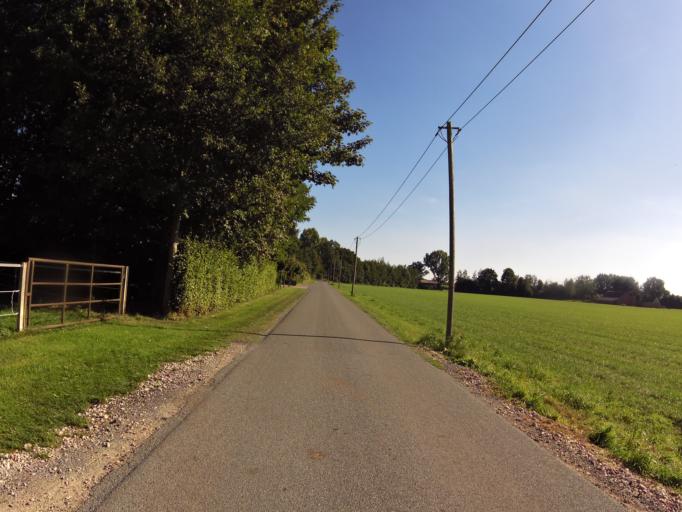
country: NL
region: Gelderland
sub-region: Gemeente Winterswijk
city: Winterswijk
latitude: 52.0514
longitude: 6.7126
